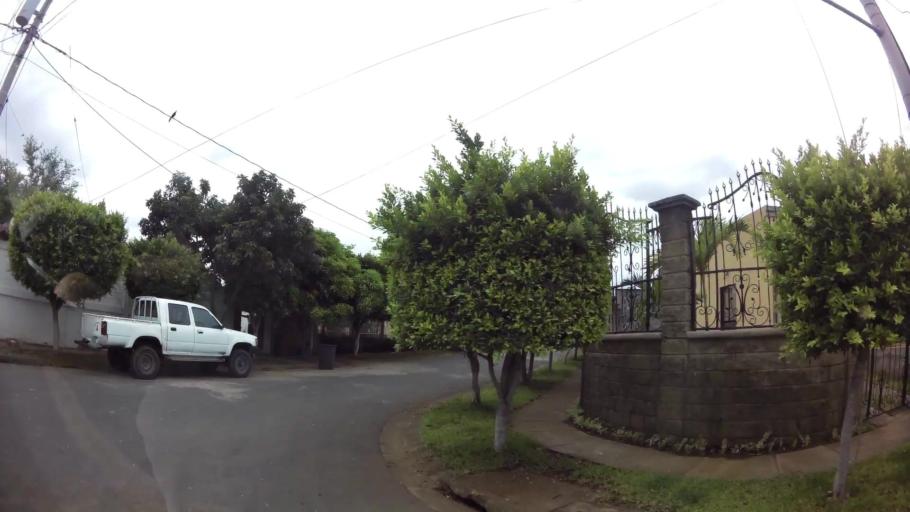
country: NI
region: Masaya
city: Ticuantepe
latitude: 12.0522
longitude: -86.1916
